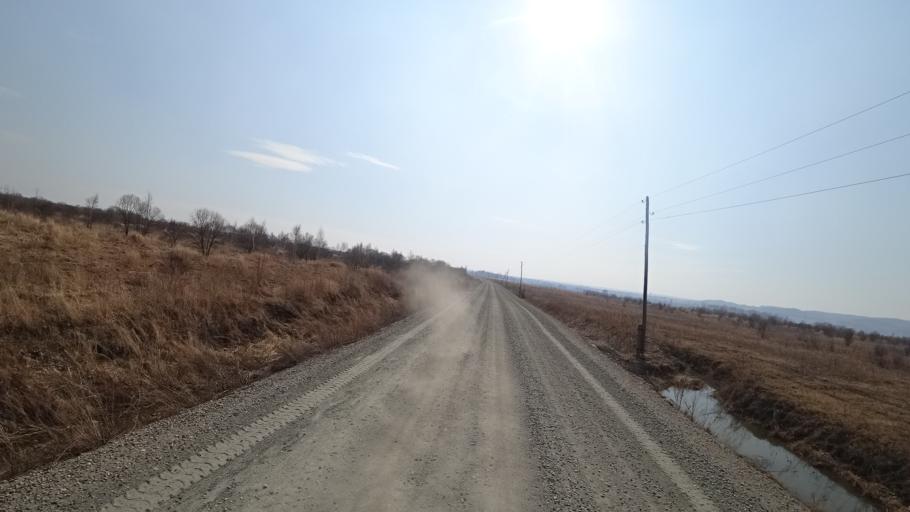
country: RU
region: Amur
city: Novobureyskiy
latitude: 49.8124
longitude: 129.9715
